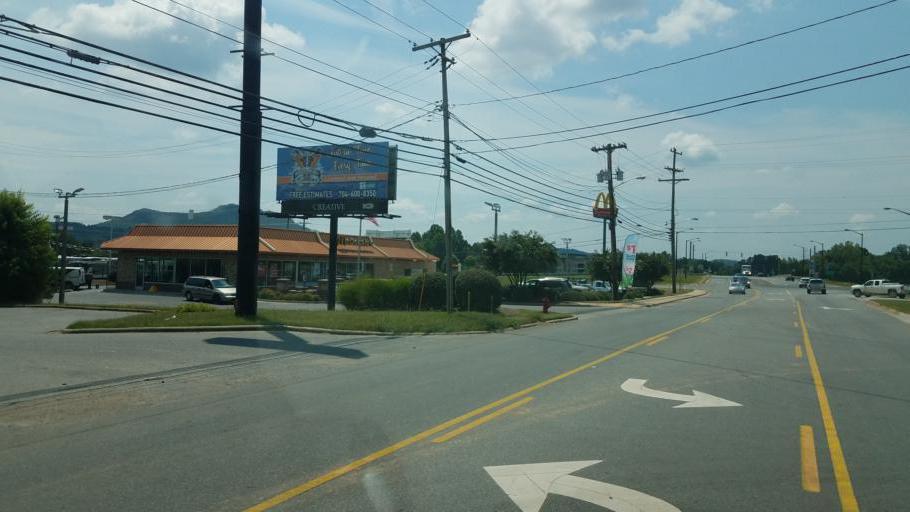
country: US
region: North Carolina
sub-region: Cleveland County
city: Kings Mountain
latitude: 35.2286
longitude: -81.3331
